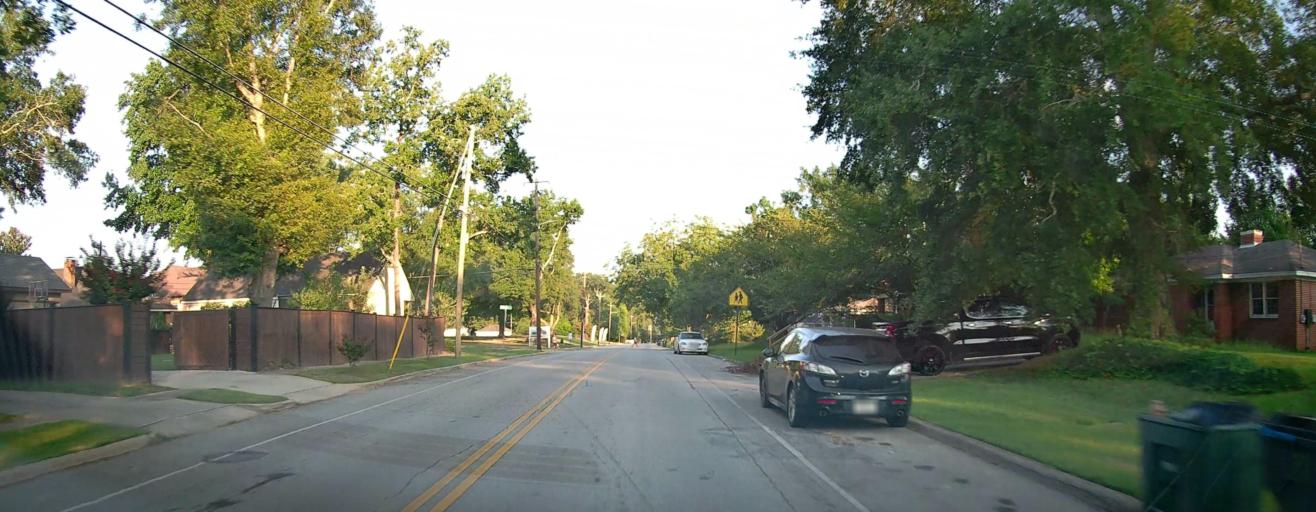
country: US
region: Georgia
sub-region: Bibb County
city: Macon
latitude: 32.8632
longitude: -83.6874
